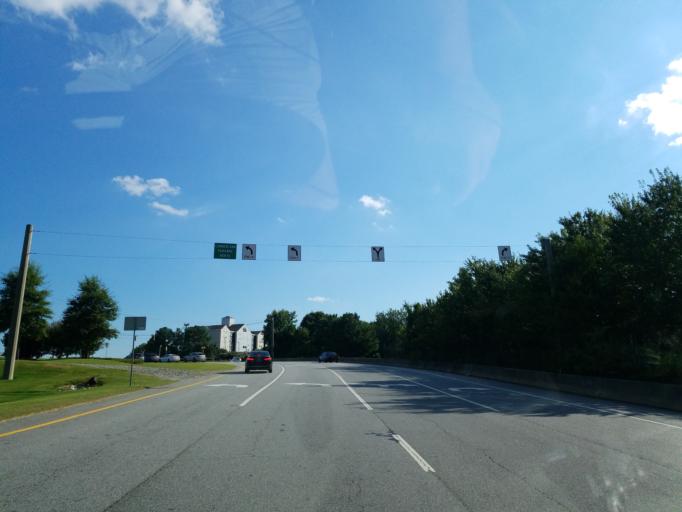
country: US
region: Georgia
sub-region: Cobb County
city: Vinings
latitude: 33.8648
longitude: -84.4804
